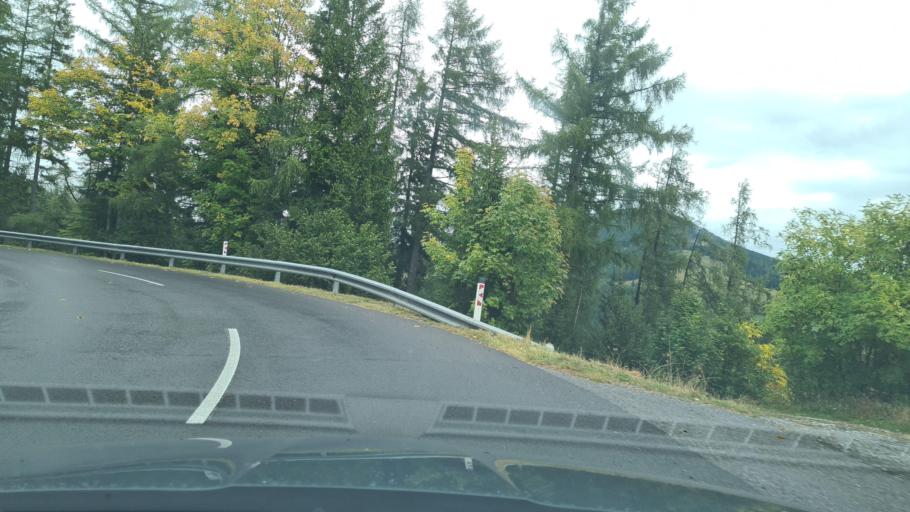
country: AT
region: Styria
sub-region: Politischer Bezirk Weiz
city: Passail
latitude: 47.3301
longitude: 15.4755
